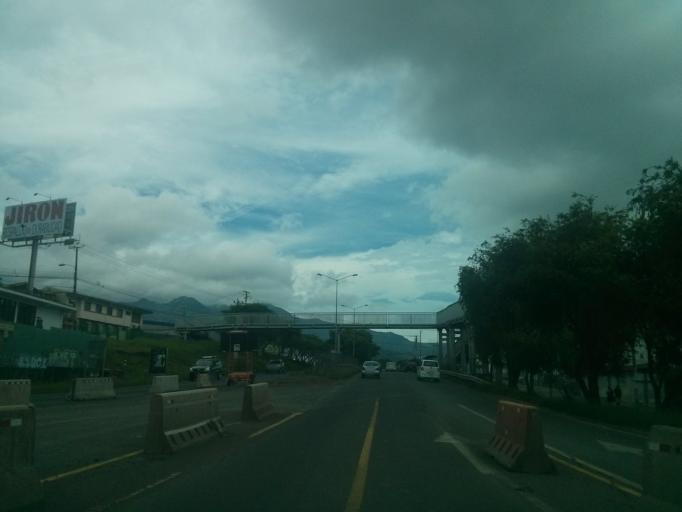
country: CR
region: San Jose
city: Alajuelita
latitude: 9.9113
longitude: -84.0815
